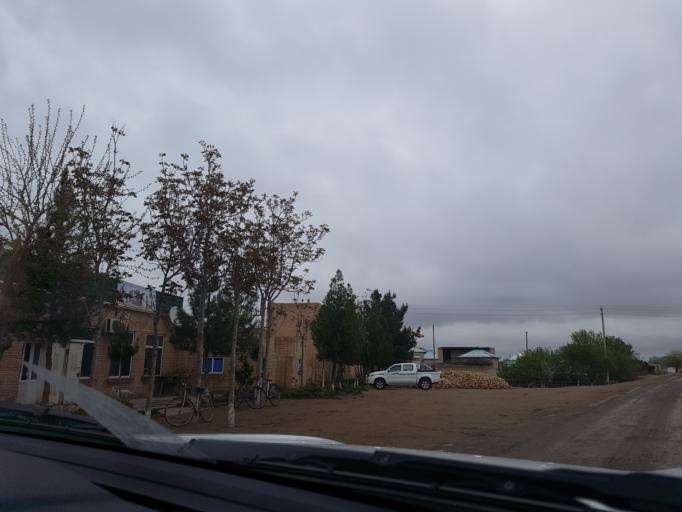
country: TM
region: Lebap
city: Sayat
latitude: 38.4569
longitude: 64.3781
